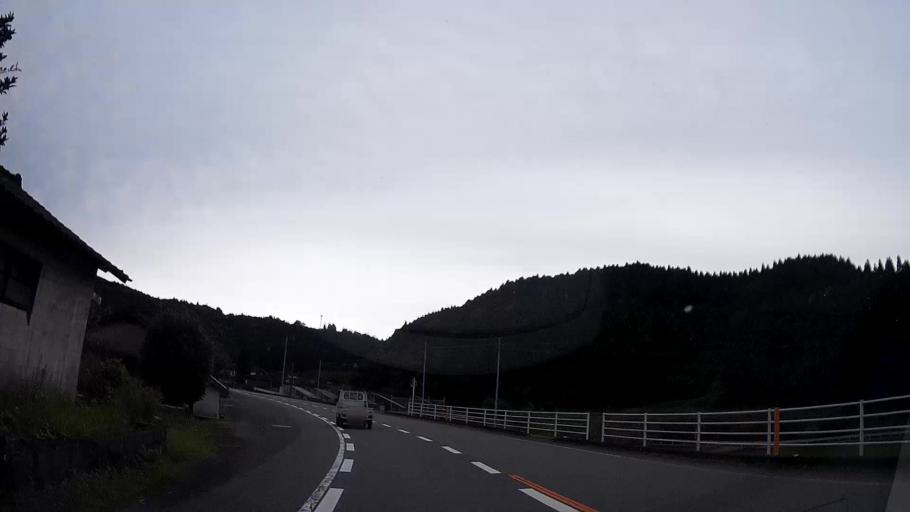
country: JP
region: Kumamoto
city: Kikuchi
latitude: 33.0155
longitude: 130.8743
